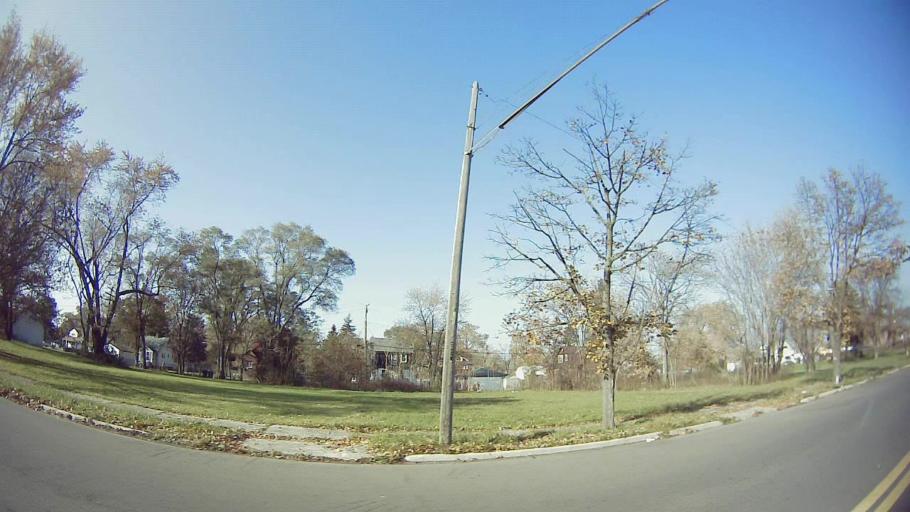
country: US
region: Michigan
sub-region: Wayne County
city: Dearborn
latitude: 42.3786
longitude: -83.1682
